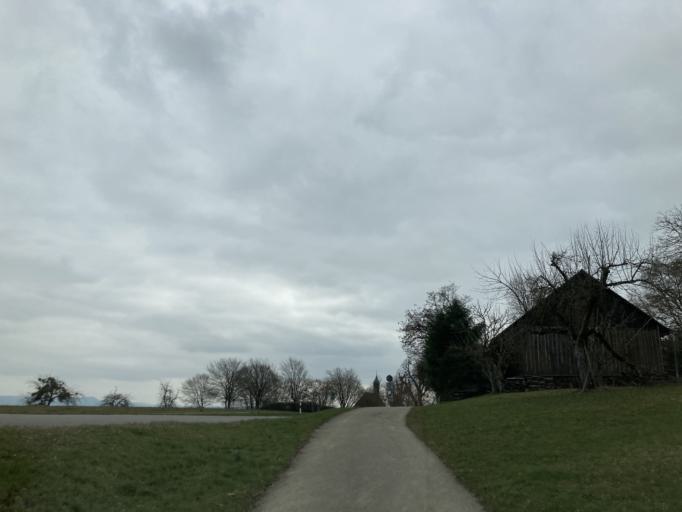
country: DE
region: Baden-Wuerttemberg
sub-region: Tuebingen Region
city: Hirrlingen
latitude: 48.4279
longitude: 8.8488
